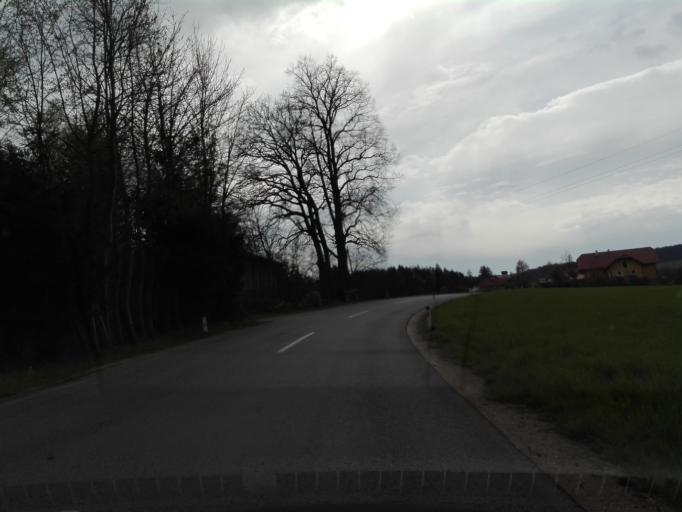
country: AT
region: Upper Austria
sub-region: Politischer Bezirk Rohrbach
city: Atzesberg
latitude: 48.5512
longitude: 13.9551
